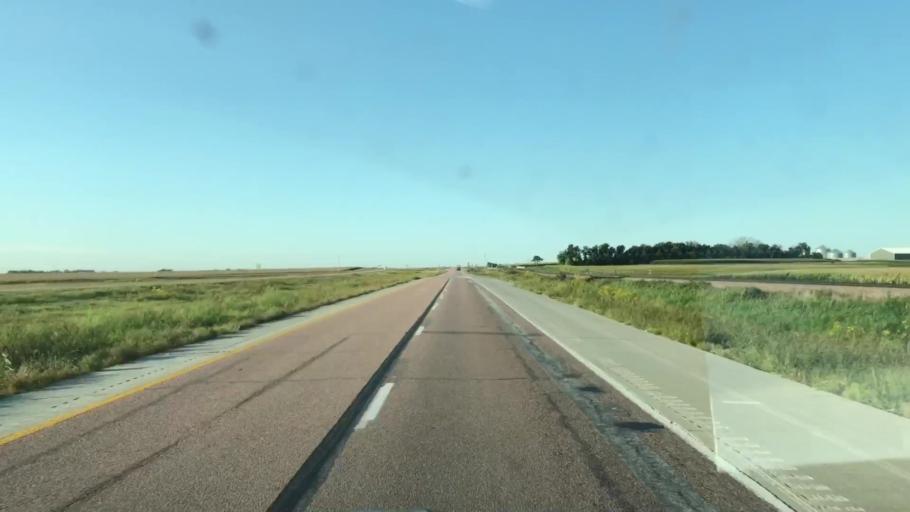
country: US
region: Iowa
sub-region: Osceola County
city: Sibley
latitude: 43.3510
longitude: -95.7716
